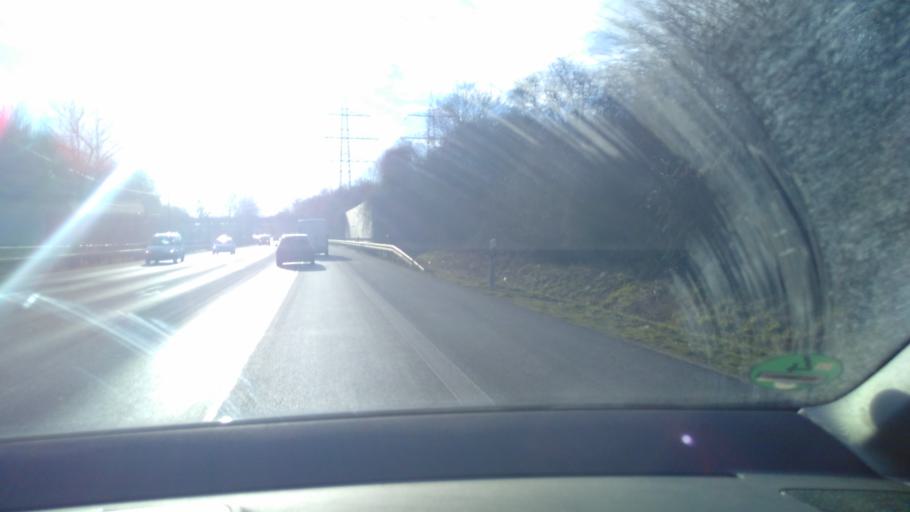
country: DE
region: North Rhine-Westphalia
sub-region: Regierungsbezirk Koln
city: Bergheim
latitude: 50.9583
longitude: 6.6161
